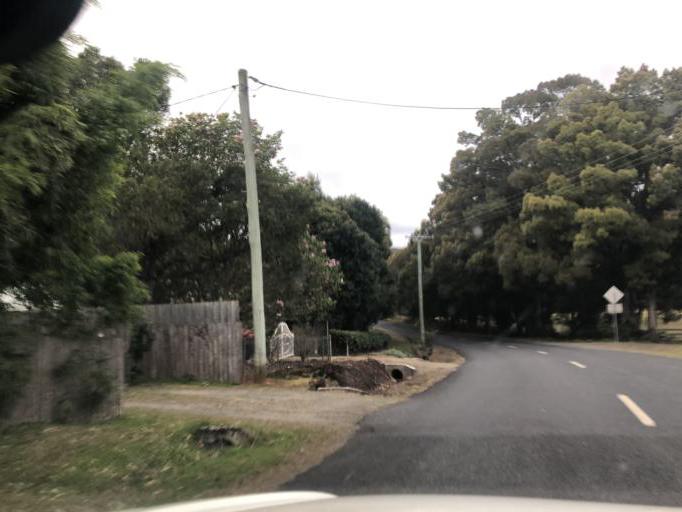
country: AU
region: New South Wales
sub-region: Coffs Harbour
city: Coffs Harbour
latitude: -30.2561
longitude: 153.0445
